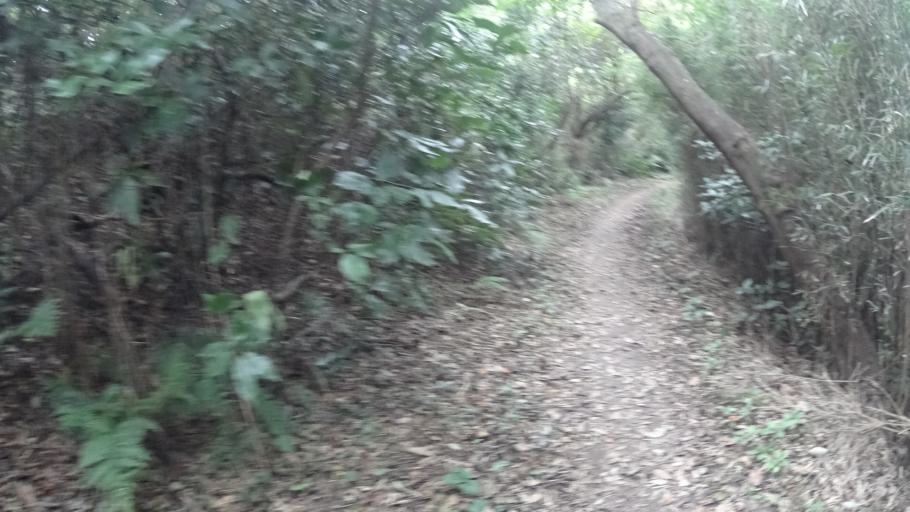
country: JP
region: Kanagawa
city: Zushi
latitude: 35.2894
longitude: 139.6104
